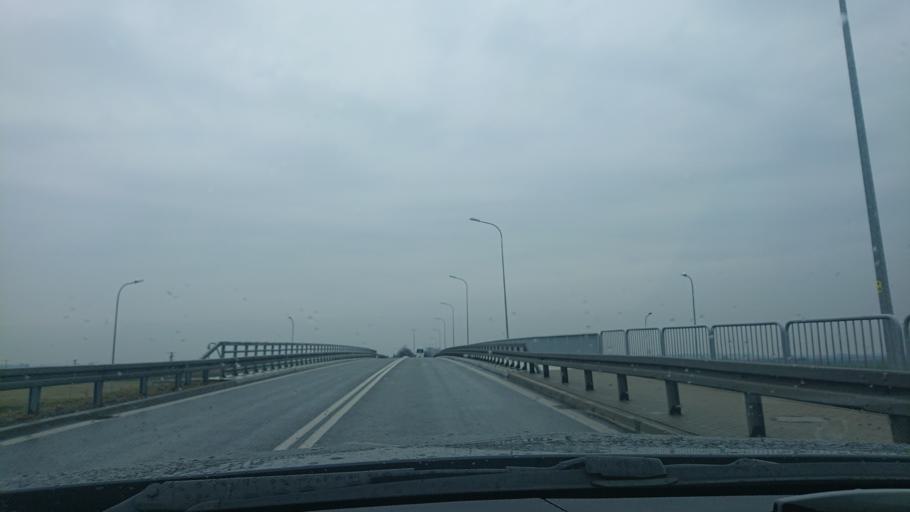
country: PL
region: Greater Poland Voivodeship
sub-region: Powiat gnieznienski
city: Gniezno
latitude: 52.5545
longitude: 17.5426
